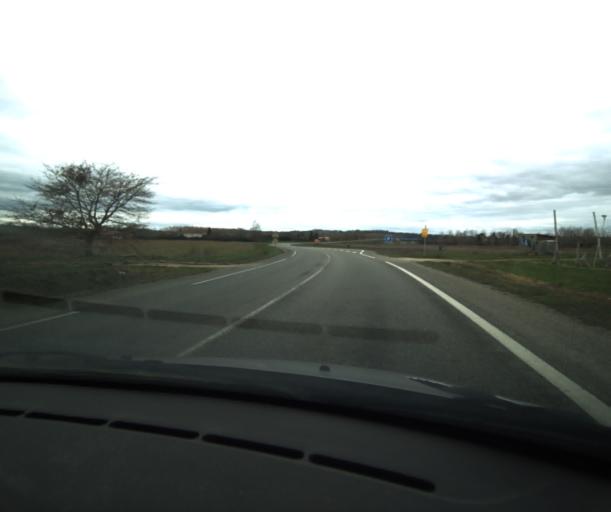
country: FR
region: Midi-Pyrenees
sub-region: Departement du Tarn-et-Garonne
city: Moissac
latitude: 44.0856
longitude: 1.1170
